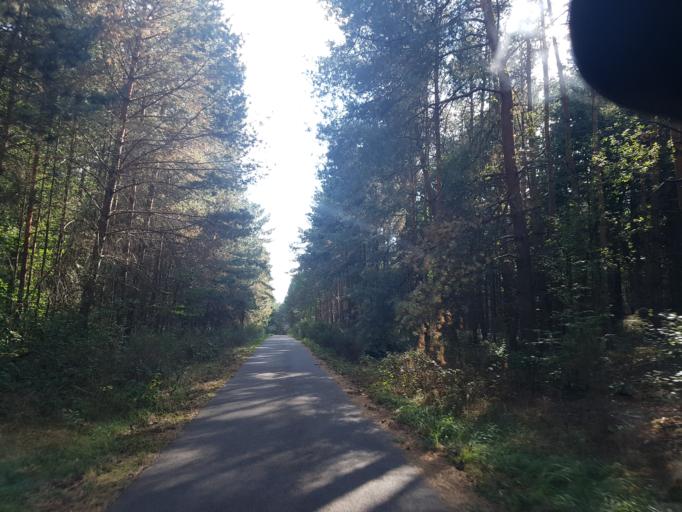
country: DE
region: Brandenburg
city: Gorzke
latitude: 52.0526
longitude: 12.2953
